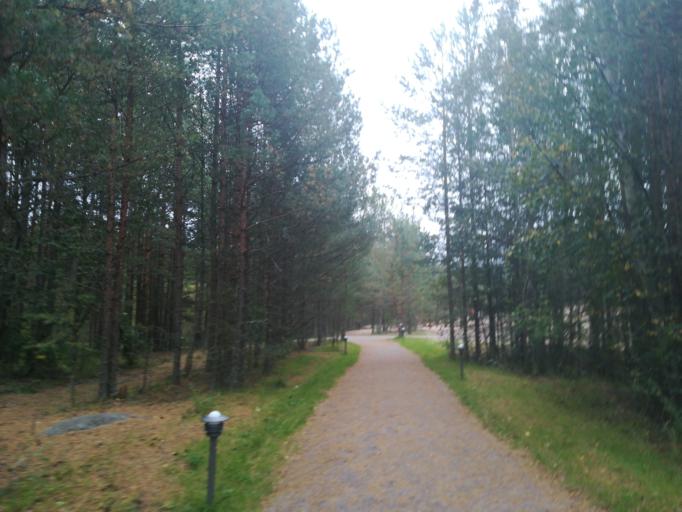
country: RU
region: Leningrad
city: Priozersk
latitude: 61.0430
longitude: 30.1803
